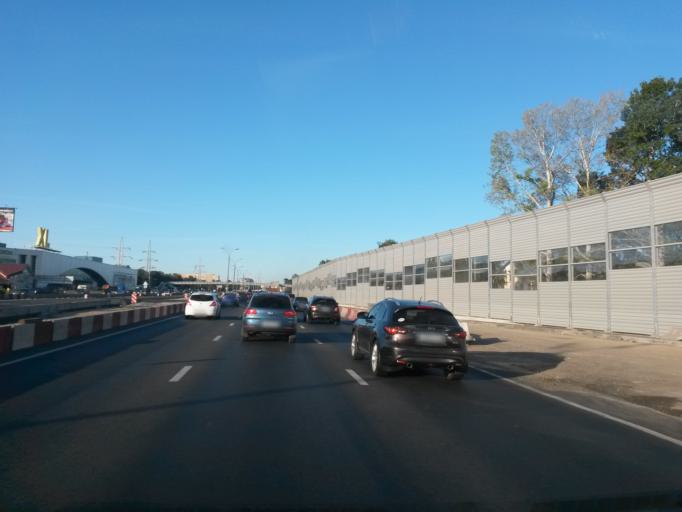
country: RU
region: Moskovskaya
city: Druzhba
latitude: 55.8944
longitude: 37.7468
